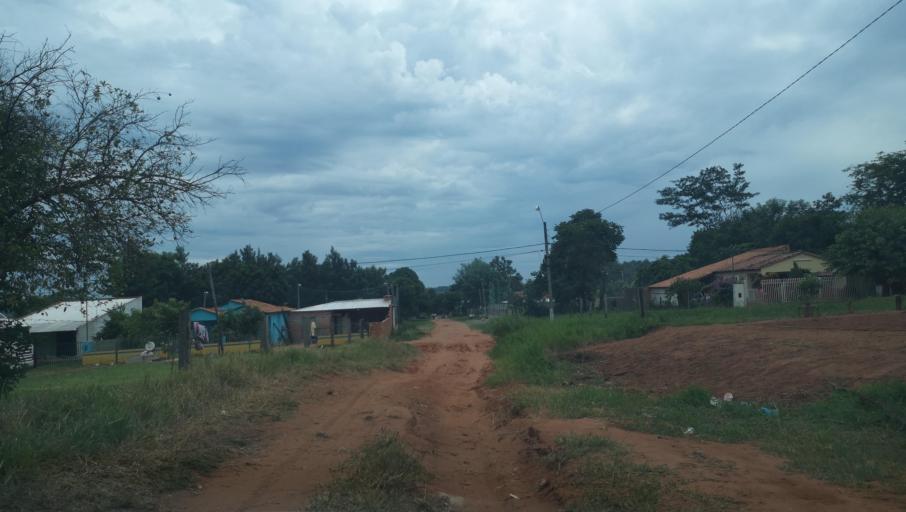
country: PY
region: San Pedro
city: Capiibary
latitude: -24.7229
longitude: -56.0134
